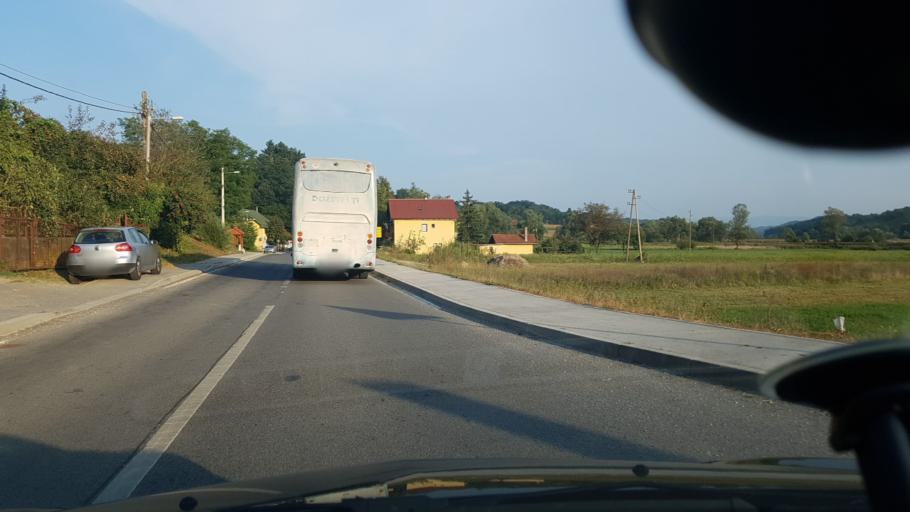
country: HR
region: Krapinsko-Zagorska
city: Pregrada
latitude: 46.1432
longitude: 15.7876
